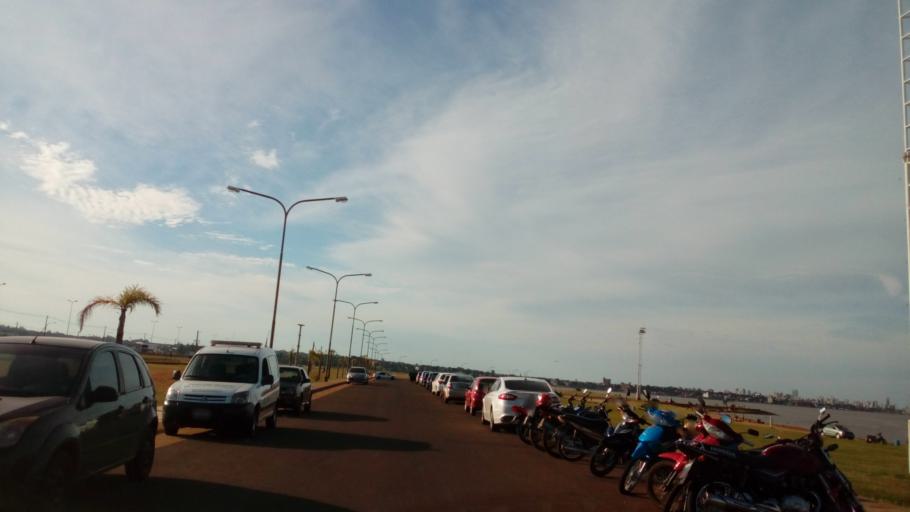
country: AR
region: Misiones
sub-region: Departamento de Capital
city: Posadas
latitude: -27.4194
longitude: -55.8792
